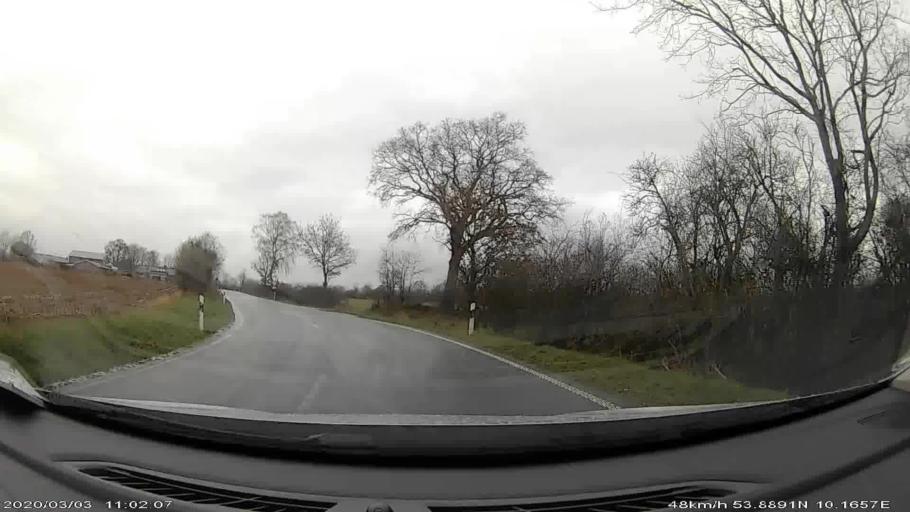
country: DE
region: Schleswig-Holstein
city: Todesfelde
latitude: 53.8913
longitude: 10.1660
